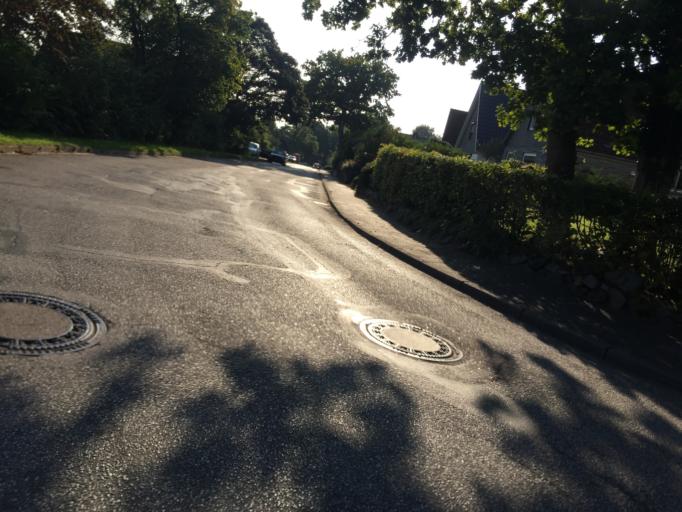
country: DE
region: Schleswig-Holstein
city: Oelixdorf
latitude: 53.9289
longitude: 9.5455
